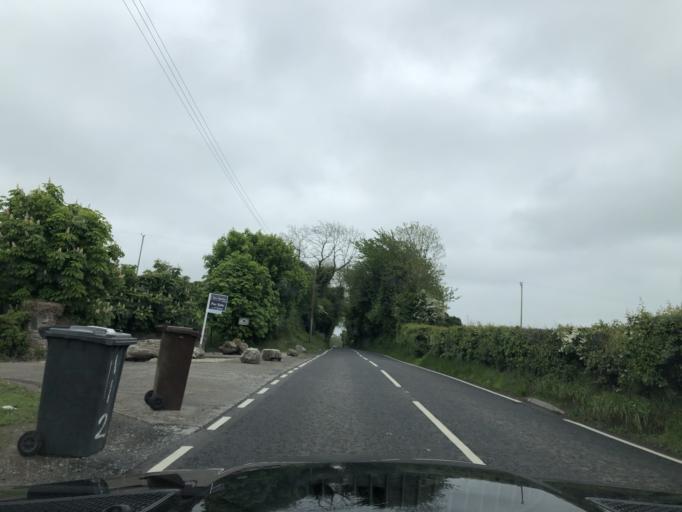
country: GB
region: Northern Ireland
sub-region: Down District
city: Downpatrick
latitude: 54.3501
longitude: -5.6915
